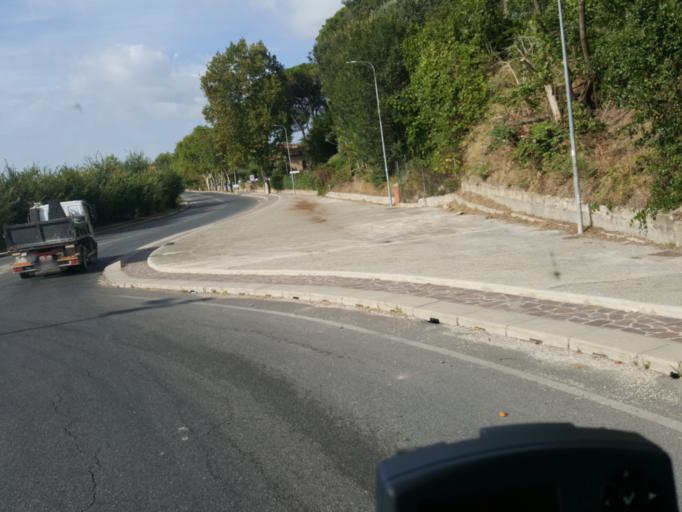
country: IT
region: Latium
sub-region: Citta metropolitana di Roma Capitale
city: Girardi-Bellavista-Terrazze
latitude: 42.1000
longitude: 12.5805
